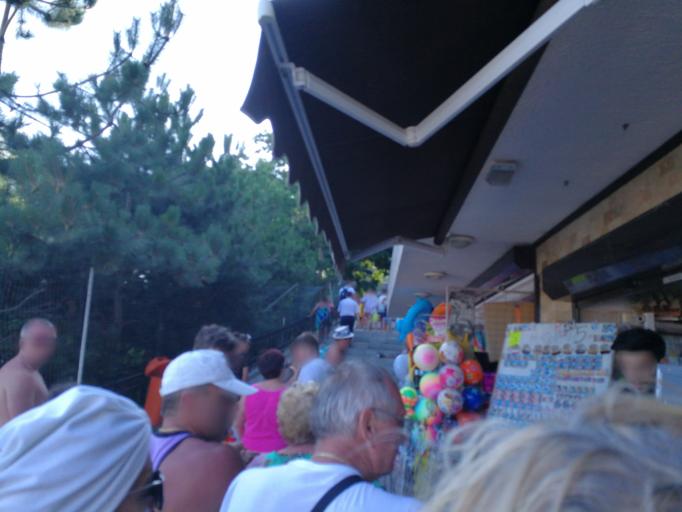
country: RO
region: Constanta
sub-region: Oras Eforie
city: Eforie Nord
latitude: 44.0625
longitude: 28.6389
